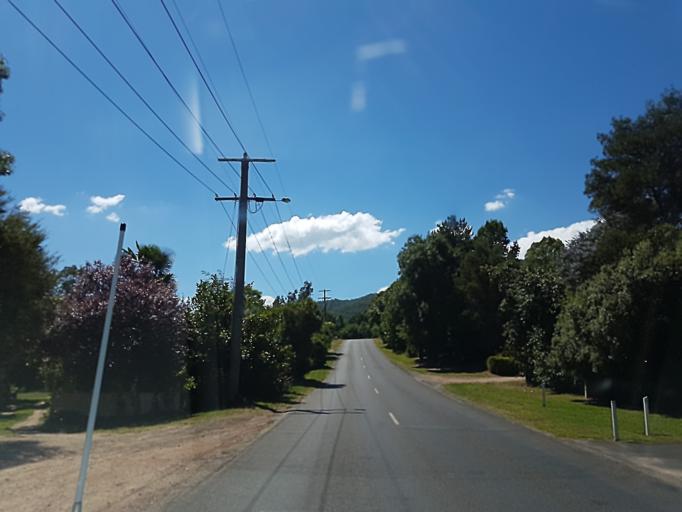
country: AU
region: Victoria
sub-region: Alpine
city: Mount Beauty
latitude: -36.7633
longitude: 146.9819
